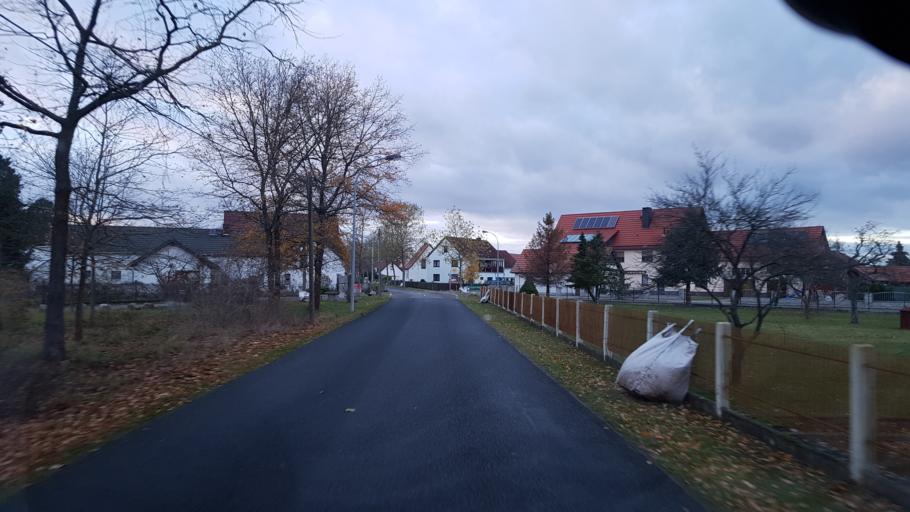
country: DE
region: Brandenburg
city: Tettau
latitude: 51.4285
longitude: 13.7353
